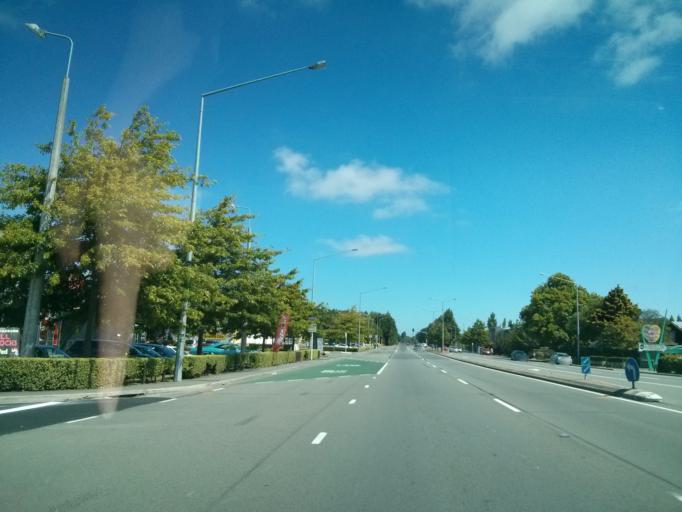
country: NZ
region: Canterbury
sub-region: Christchurch City
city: Christchurch
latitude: -43.4586
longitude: 172.6237
